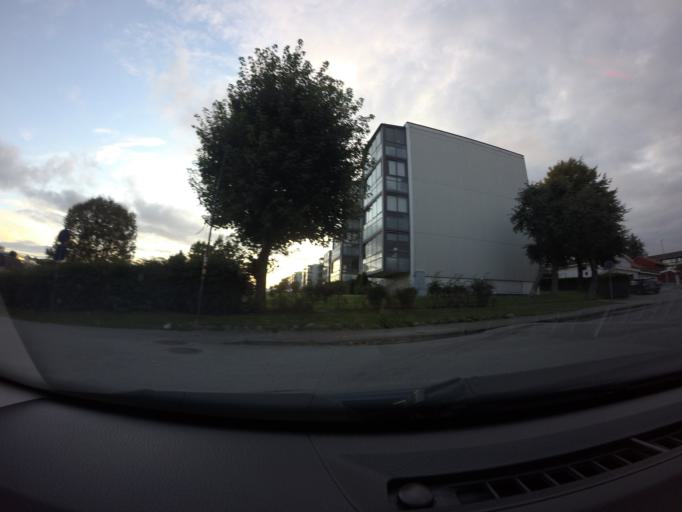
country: NO
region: Rogaland
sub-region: Stavanger
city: Stavanger
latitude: 58.9508
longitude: 5.7400
